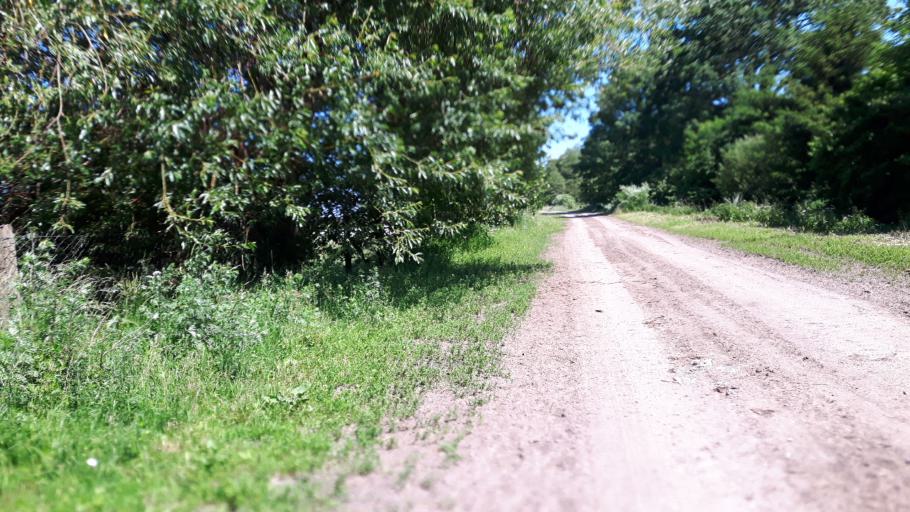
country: PL
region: Pomeranian Voivodeship
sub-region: Powiat slupski
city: Glowczyce
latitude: 54.6410
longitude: 17.3777
